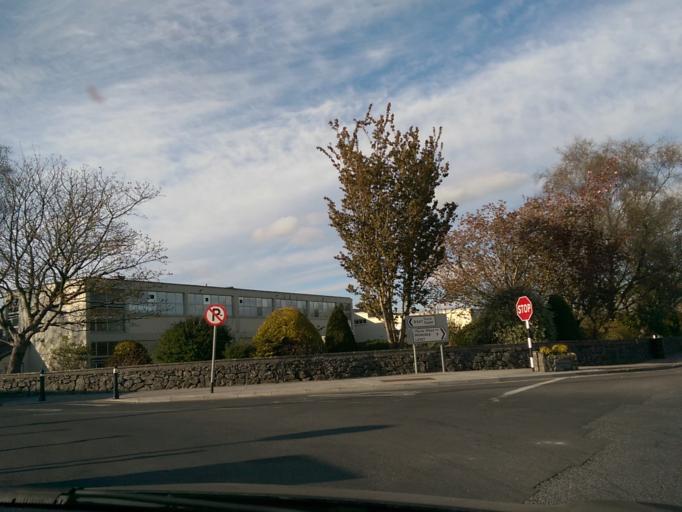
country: IE
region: Connaught
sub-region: County Galway
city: Athenry
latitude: 53.3007
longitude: -8.7456
